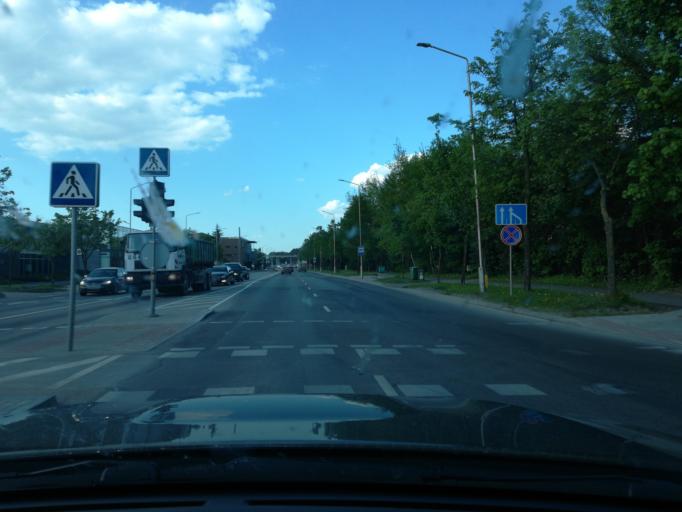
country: LT
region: Kauno apskritis
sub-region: Kaunas
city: Eiguliai
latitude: 54.9310
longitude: 23.9169
